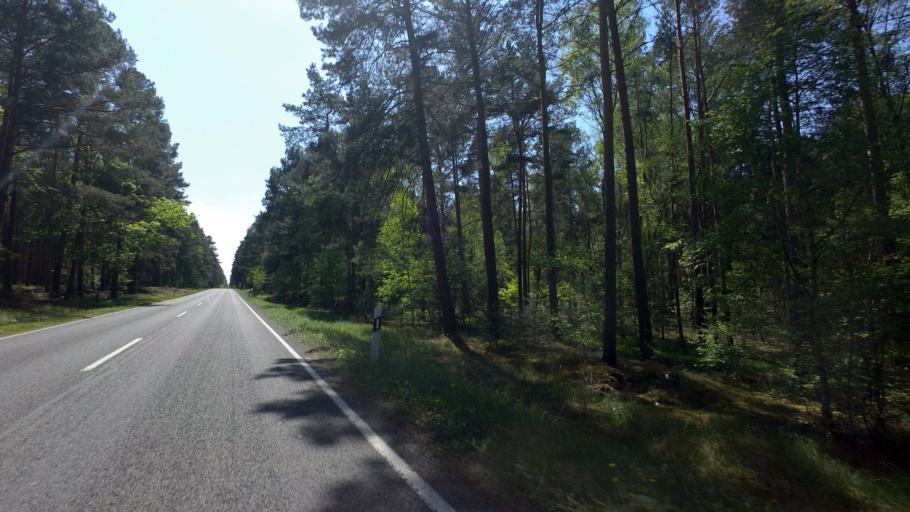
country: DE
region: Brandenburg
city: Gross Koris
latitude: 52.2090
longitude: 13.6900
